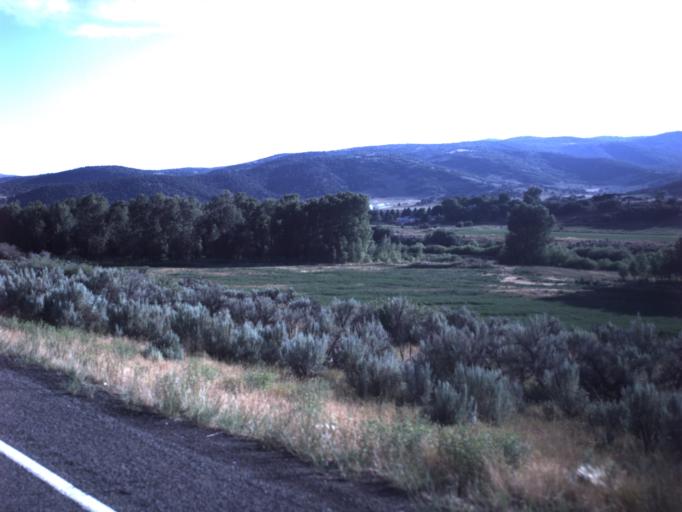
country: US
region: Utah
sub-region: Utah County
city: Woodland Hills
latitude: 39.9286
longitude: -111.5435
